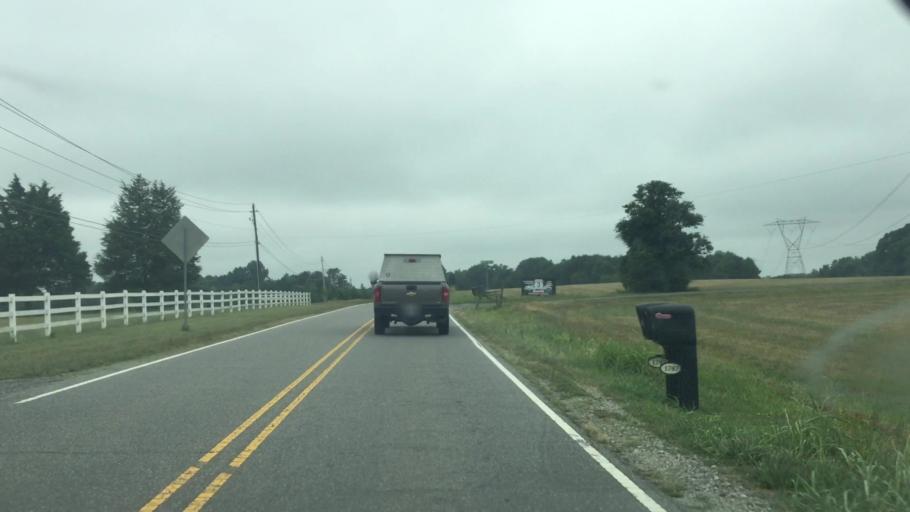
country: US
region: North Carolina
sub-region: Iredell County
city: Mooresville
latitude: 35.5383
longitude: -80.7682
